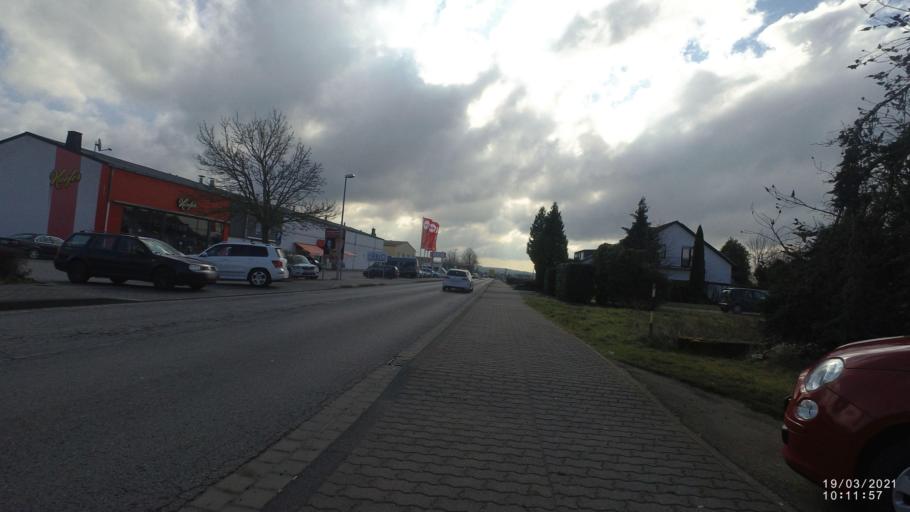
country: DE
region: Rheinland-Pfalz
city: Mendig
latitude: 50.3675
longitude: 7.2912
